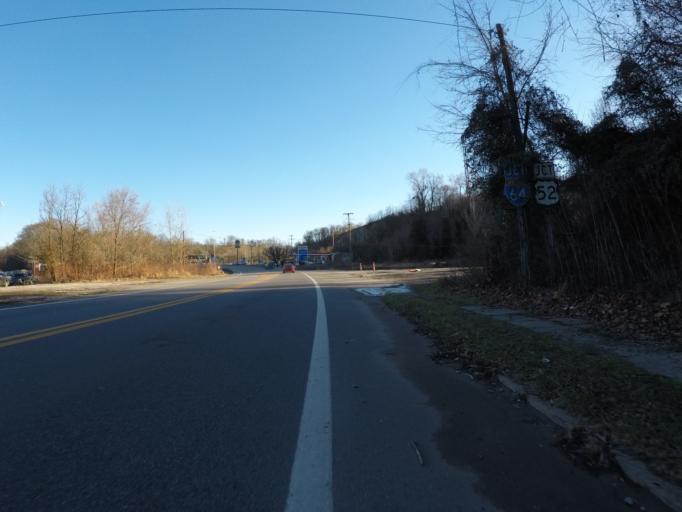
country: US
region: West Virginia
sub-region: Wayne County
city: Kenova
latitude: 38.3939
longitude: -82.5773
